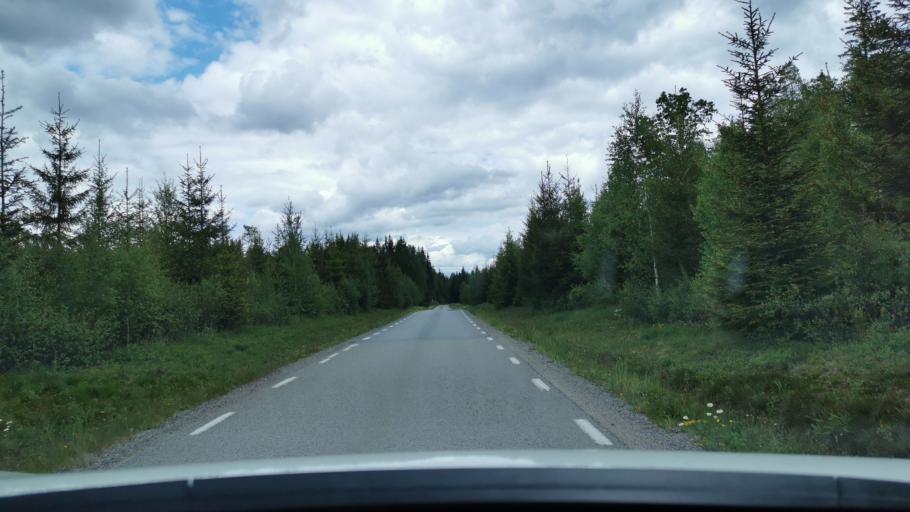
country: SE
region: Vaestra Goetaland
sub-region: Bengtsfors Kommun
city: Dals Langed
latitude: 58.8094
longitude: 12.3253
